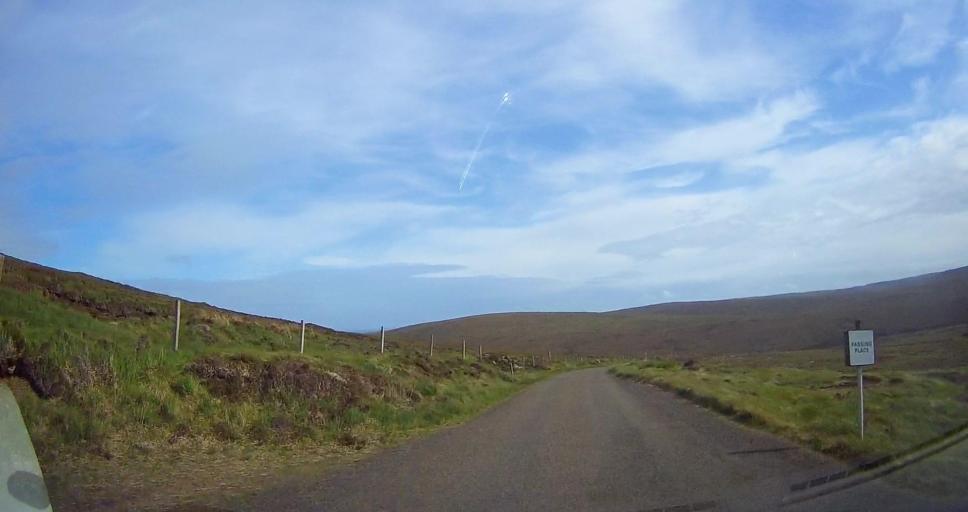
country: GB
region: Scotland
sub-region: Orkney Islands
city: Stromness
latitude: 58.8785
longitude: -3.2477
